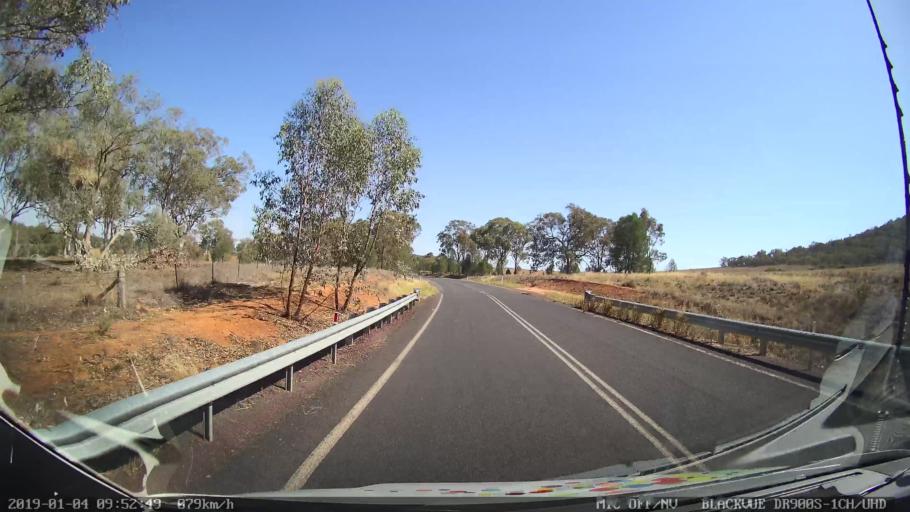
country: AU
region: New South Wales
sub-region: Cabonne
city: Canowindra
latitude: -33.5592
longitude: 148.4245
